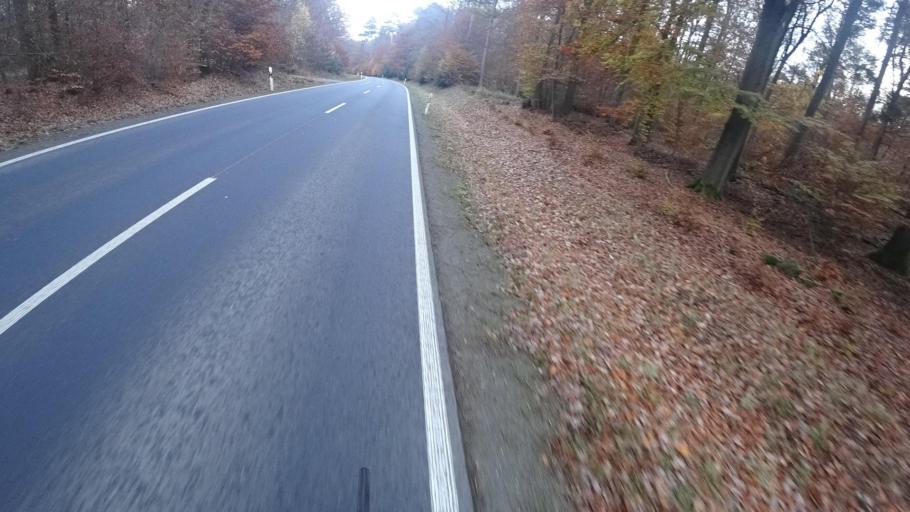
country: DE
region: Rheinland-Pfalz
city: Niederburg
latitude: 50.1306
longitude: 7.6716
